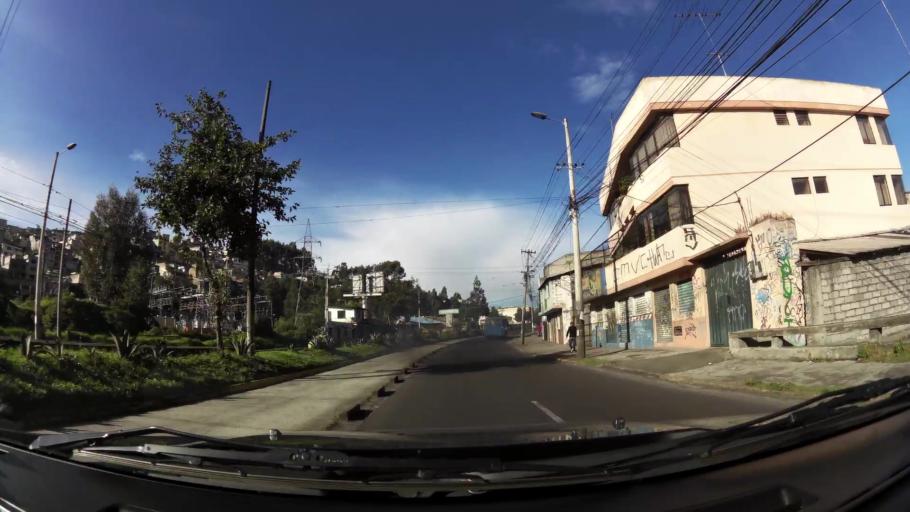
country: EC
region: Pichincha
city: Quito
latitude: -0.2753
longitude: -78.5301
